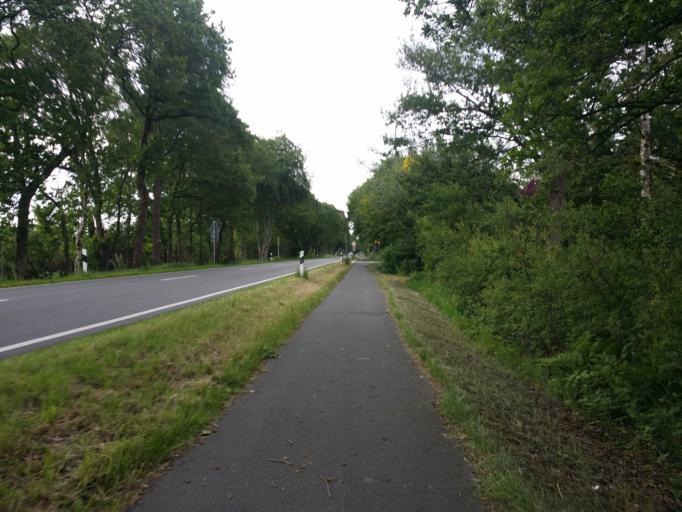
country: DE
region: Lower Saxony
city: Wittmund
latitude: 53.5517
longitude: 7.7837
